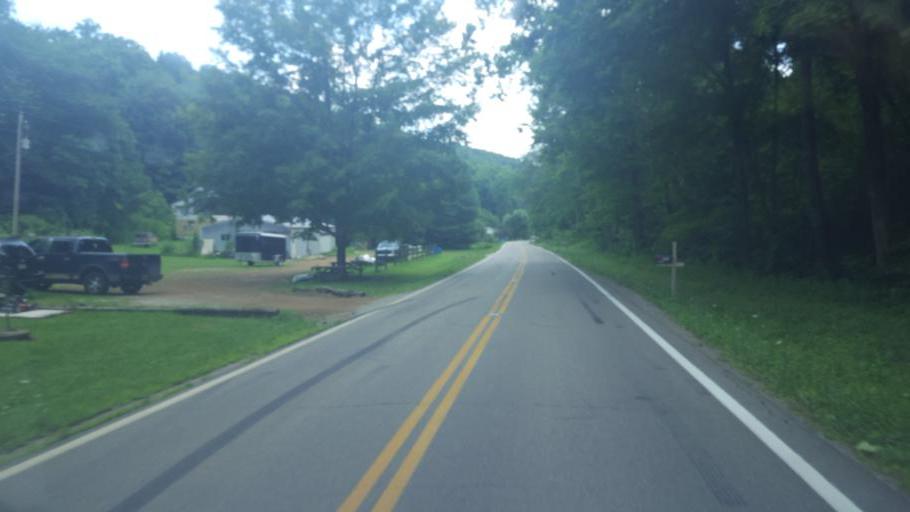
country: US
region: Ohio
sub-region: Ross County
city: Kingston
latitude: 39.4000
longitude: -82.7320
